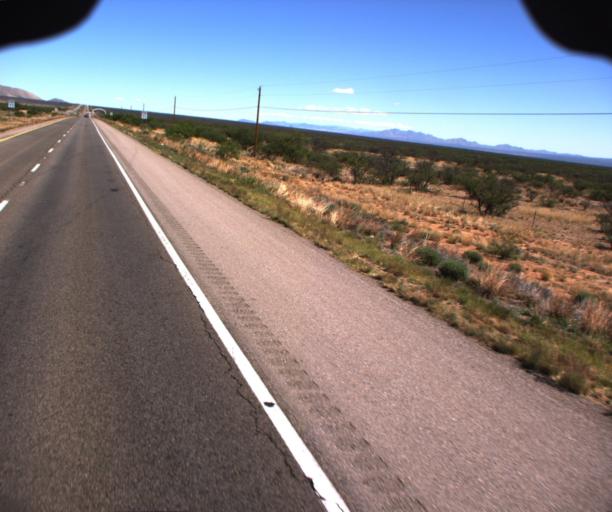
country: US
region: Arizona
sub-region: Cochise County
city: Huachuca City
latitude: 31.7371
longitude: -110.3500
